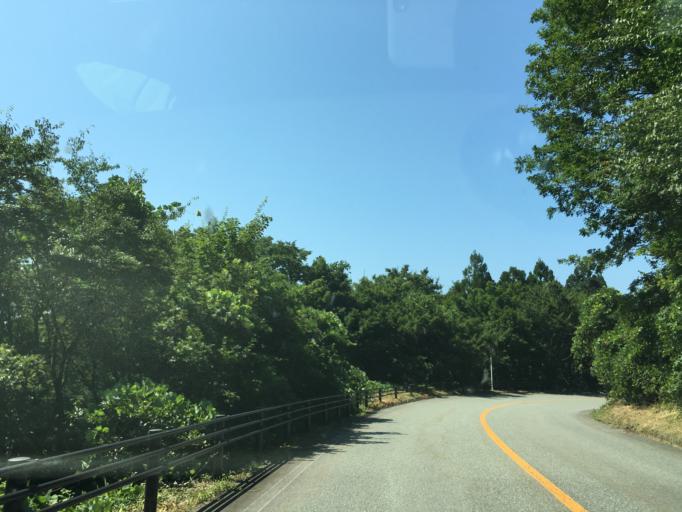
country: JP
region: Akita
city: Tenno
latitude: 39.9118
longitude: 139.7332
